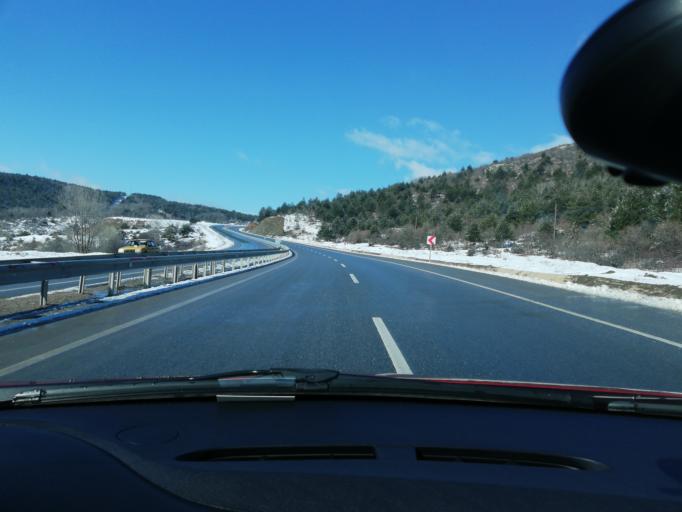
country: TR
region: Kastamonu
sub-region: Cide
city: Kastamonu
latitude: 41.3604
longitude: 33.6961
